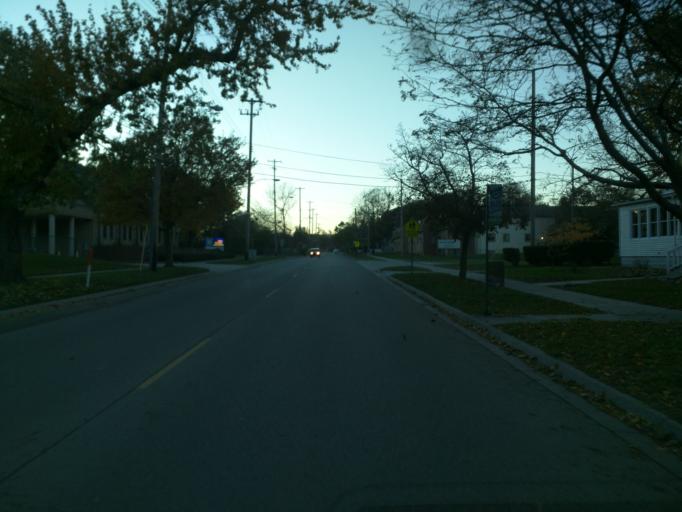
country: US
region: Michigan
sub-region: Ingham County
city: Lansing
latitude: 42.7488
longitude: -84.5586
